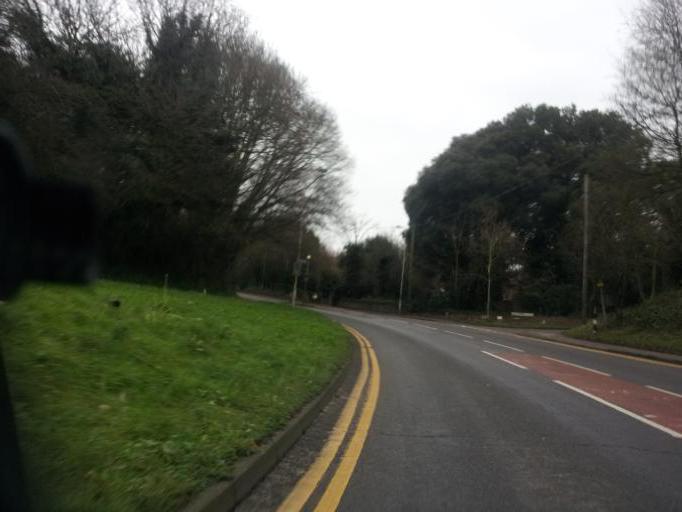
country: GB
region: England
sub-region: Kent
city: Longfield
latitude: 51.3947
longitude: 0.3019
